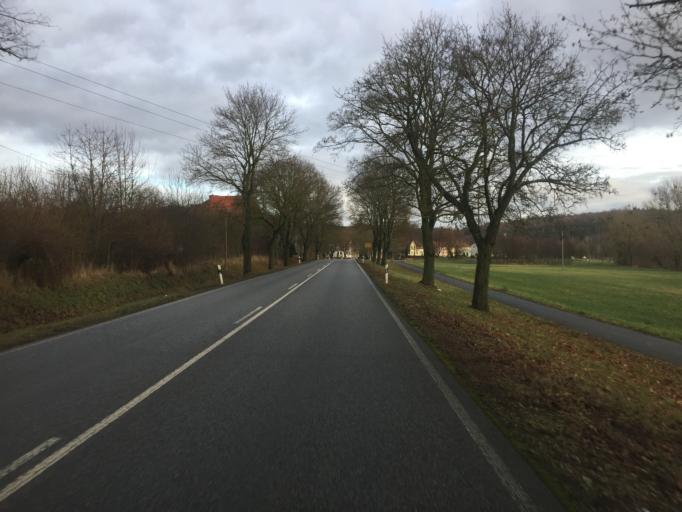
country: DE
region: Thuringia
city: Buhla
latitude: 51.4146
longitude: 10.4488
